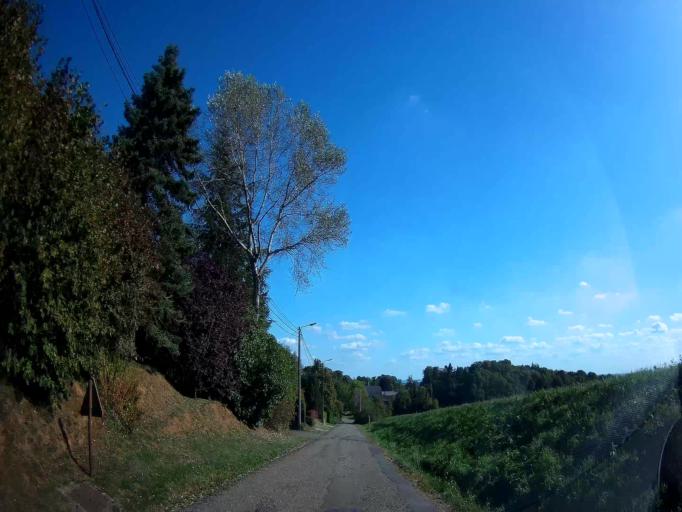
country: BE
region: Wallonia
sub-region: Province de Namur
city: Houyet
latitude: 50.2401
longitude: 4.9872
